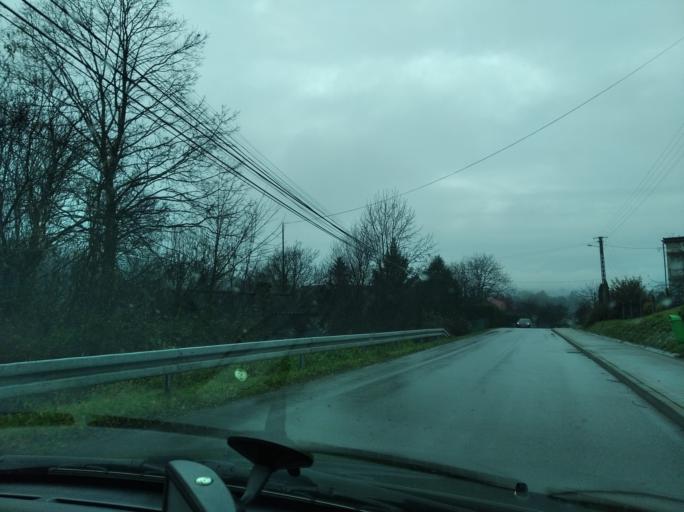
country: PL
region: Subcarpathian Voivodeship
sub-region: Powiat rzeszowski
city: Lubenia
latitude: 49.9316
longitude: 21.9236
